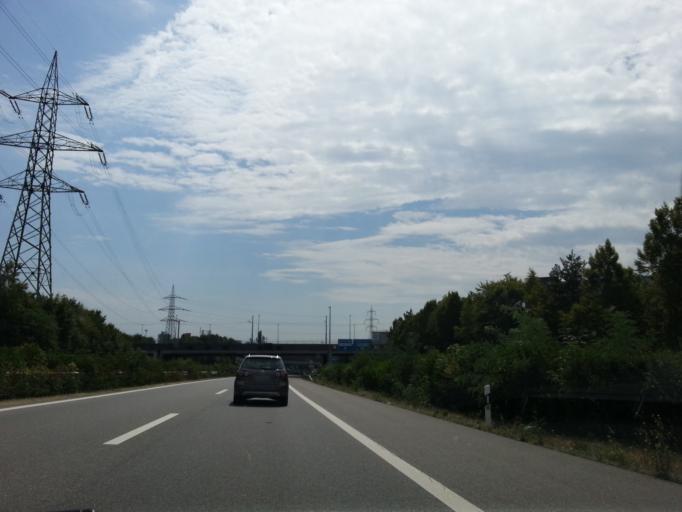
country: CH
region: Geneva
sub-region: Geneva
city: Les Avanchets
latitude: 46.2226
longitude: 6.1013
